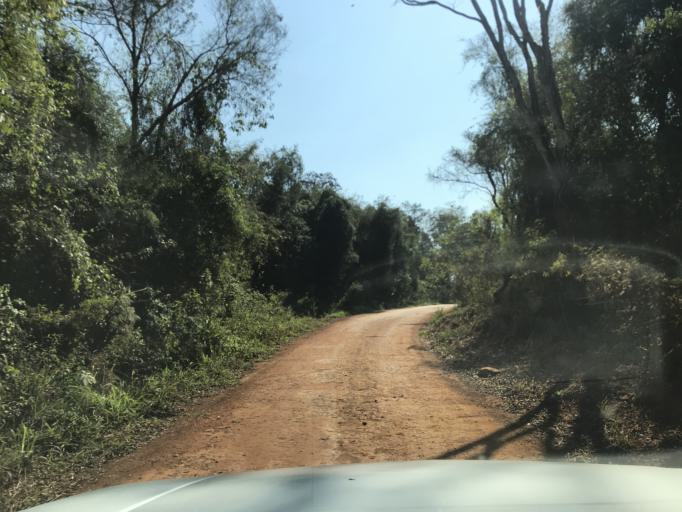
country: BR
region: Parana
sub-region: Palotina
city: Palotina
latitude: -24.2203
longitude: -53.7353
